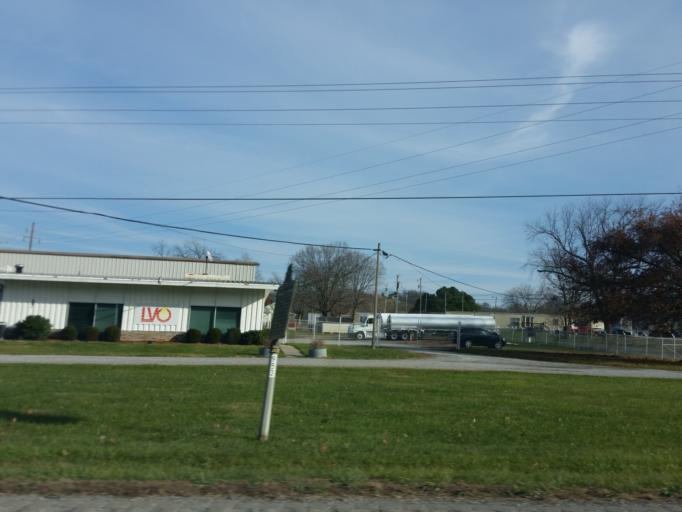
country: US
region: Kentucky
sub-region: Pendleton County
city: Falmouth
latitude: 38.7629
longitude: -84.3528
